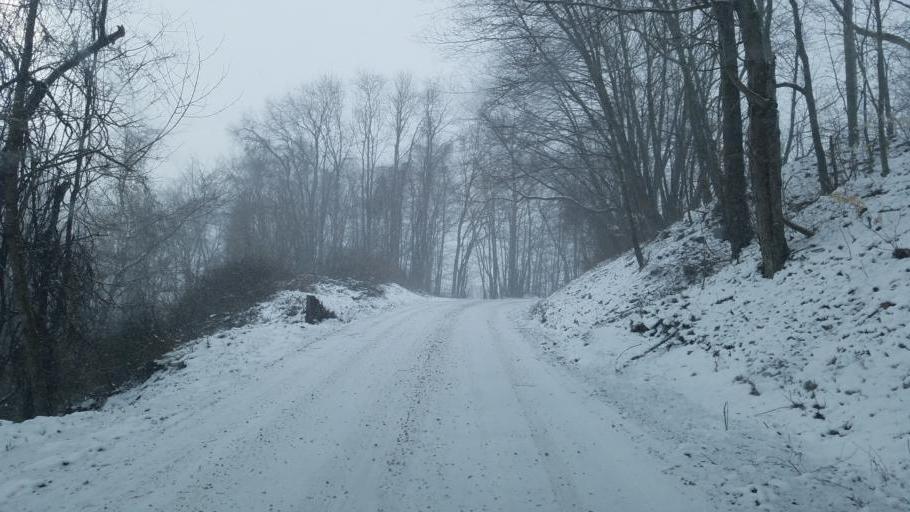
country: US
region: Pennsylvania
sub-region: Venango County
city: Sugarcreek
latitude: 41.4727
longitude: -79.9422
